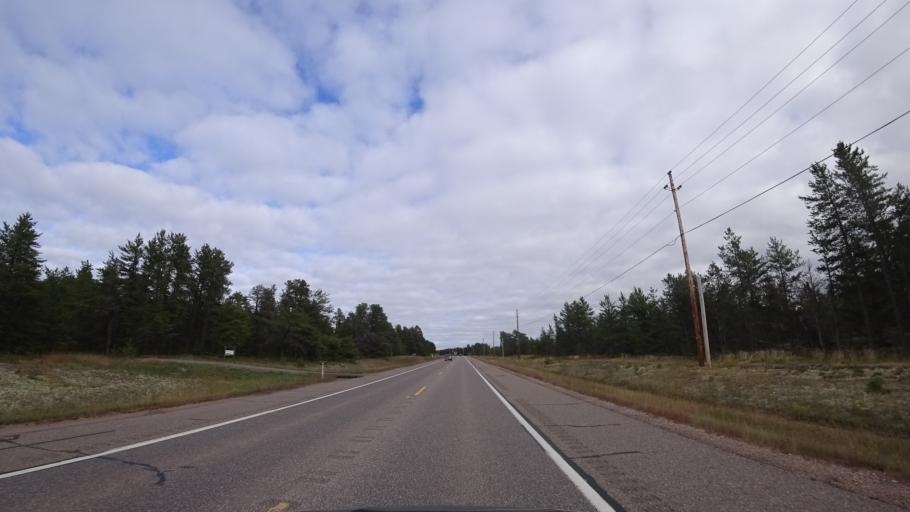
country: US
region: Michigan
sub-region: Marquette County
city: Harvey
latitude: 46.4850
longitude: -87.2567
